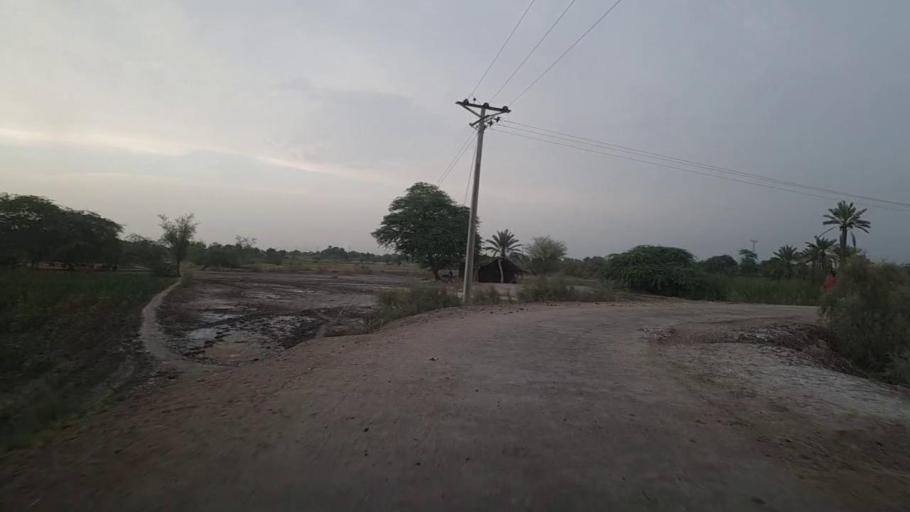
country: PK
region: Sindh
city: Karaundi
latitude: 27.0056
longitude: 68.3526
